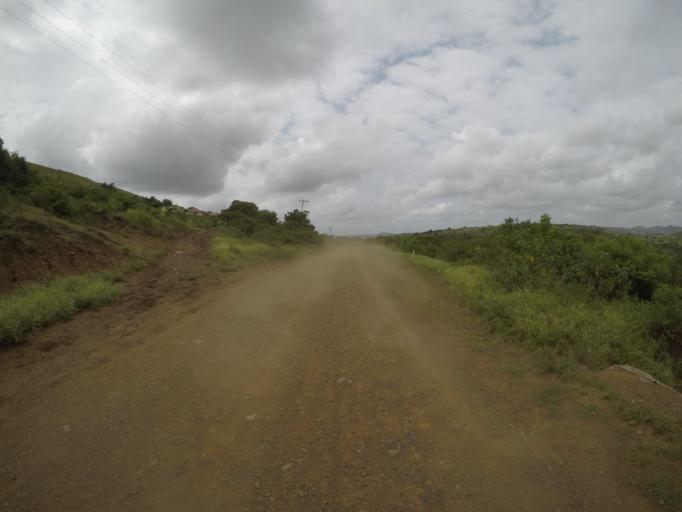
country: ZA
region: KwaZulu-Natal
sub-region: uThungulu District Municipality
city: Empangeni
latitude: -28.6089
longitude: 31.8962
